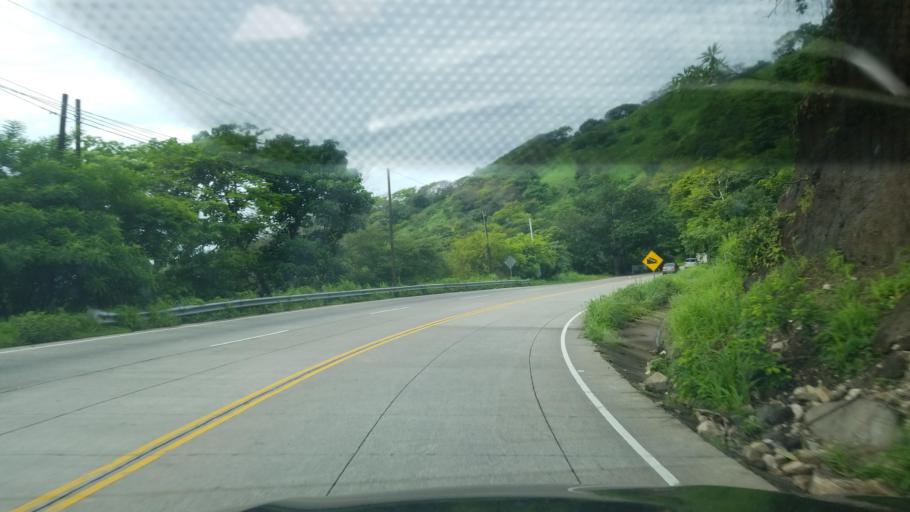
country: HN
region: Francisco Morazan
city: El Porvenir
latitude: 13.7104
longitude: -87.3179
